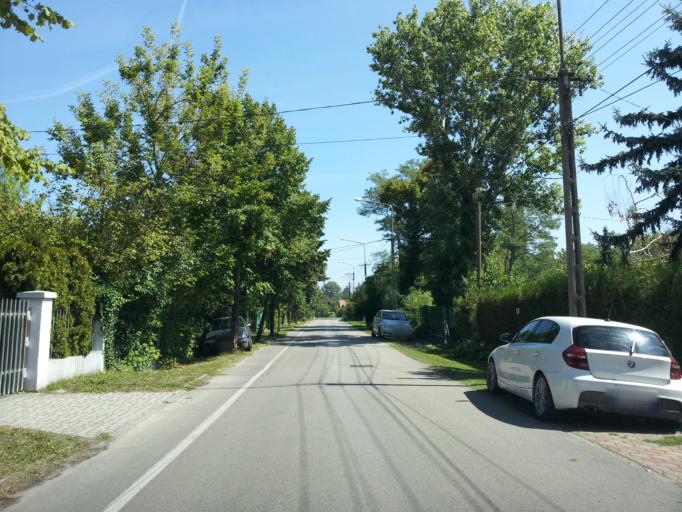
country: HU
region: Somogy
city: Zamardi
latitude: 46.8849
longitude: 17.9527
